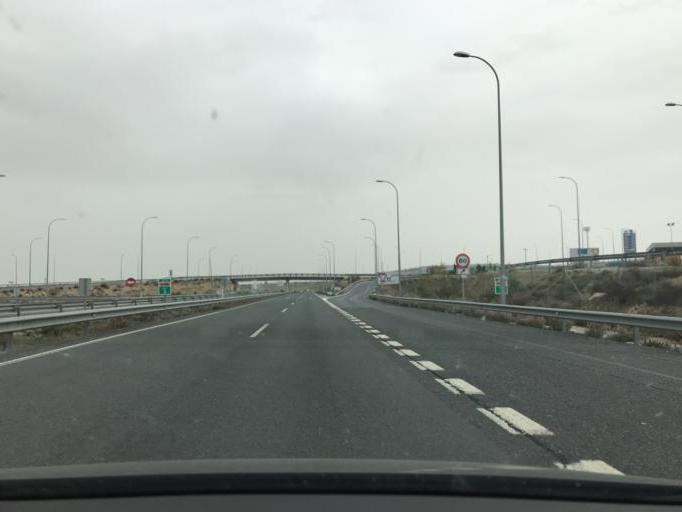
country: ES
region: Andalusia
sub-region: Provincia de Granada
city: Guadix
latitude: 37.3355
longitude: -3.0942
